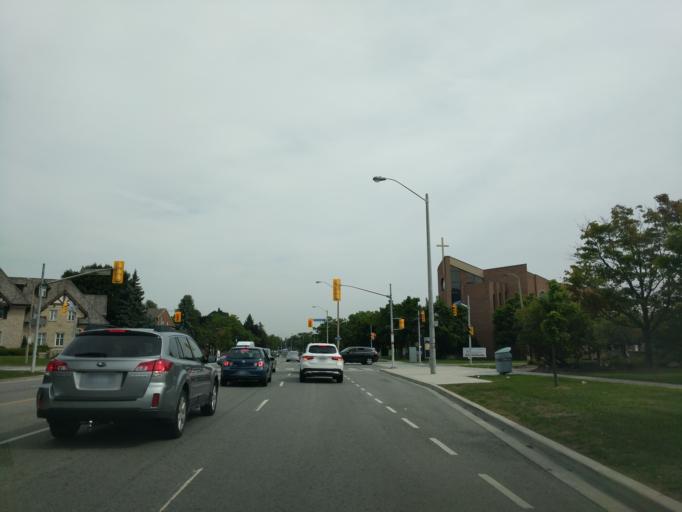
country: CA
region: Ontario
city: Markham
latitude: 43.8157
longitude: -79.3246
